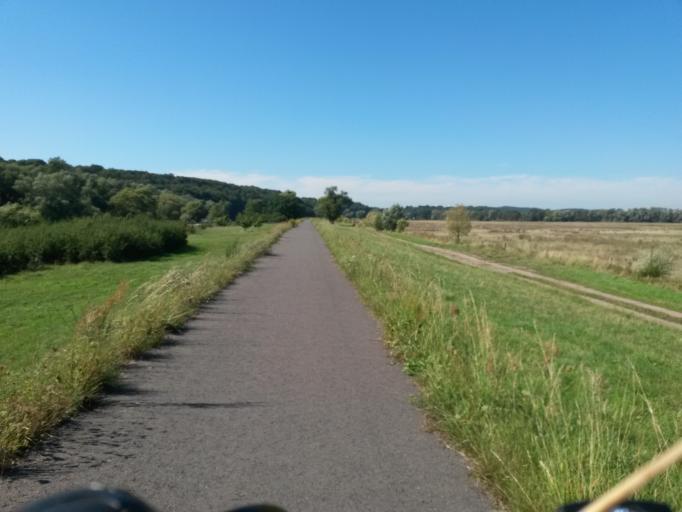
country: DE
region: Brandenburg
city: Schoneberg
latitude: 52.9386
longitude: 14.1235
